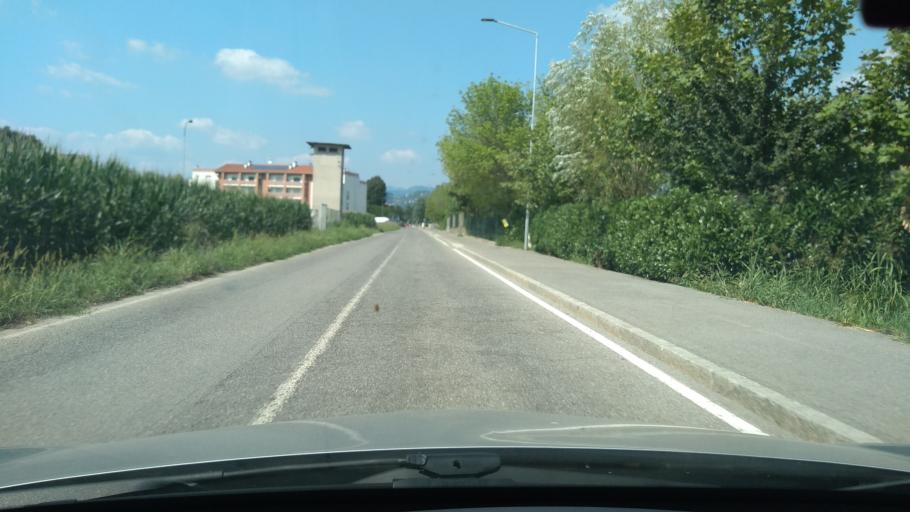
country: IT
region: Lombardy
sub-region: Provincia di Bergamo
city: Lallio
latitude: 45.6639
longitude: 9.6394
